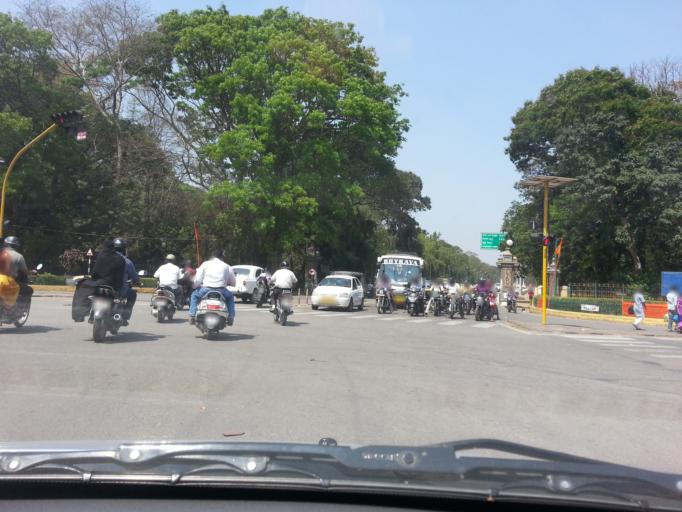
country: IN
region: Karnataka
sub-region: Mysore
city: Mysore
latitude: 12.3073
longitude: 76.6601
